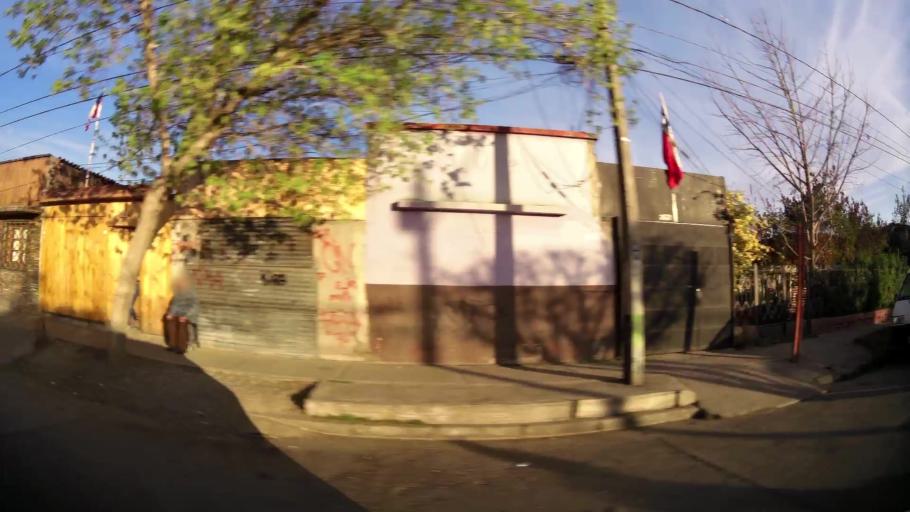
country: CL
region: Santiago Metropolitan
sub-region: Provincia de Santiago
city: Lo Prado
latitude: -33.4128
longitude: -70.7155
